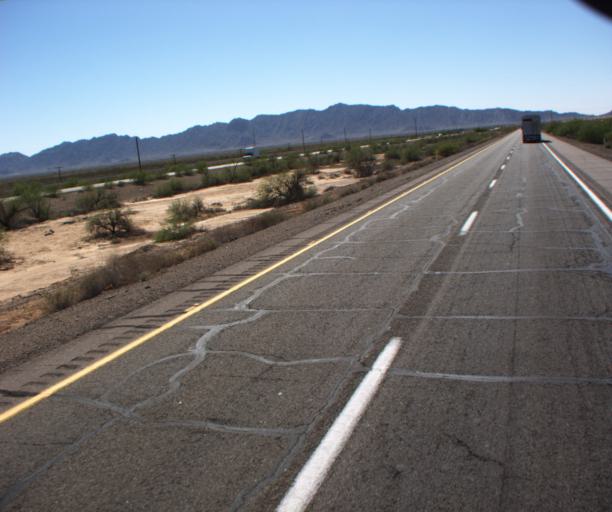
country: US
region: Arizona
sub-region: Yuma County
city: Wellton
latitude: 32.7528
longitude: -113.6569
